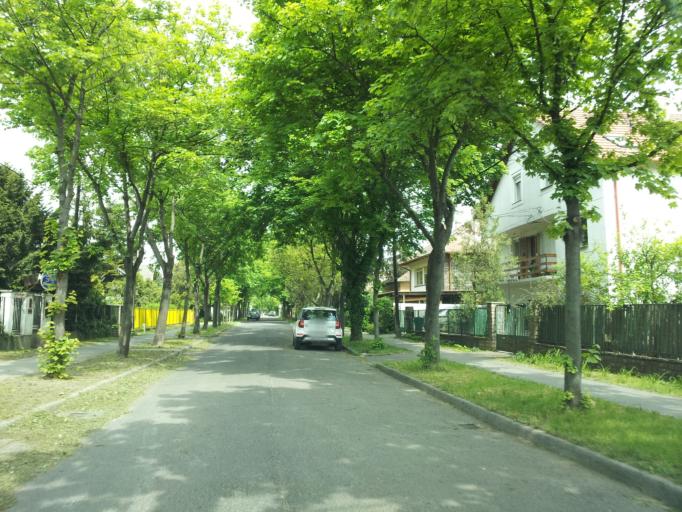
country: HU
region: Budapest
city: Budapest IV. keruelet
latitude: 47.5712
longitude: 19.0594
